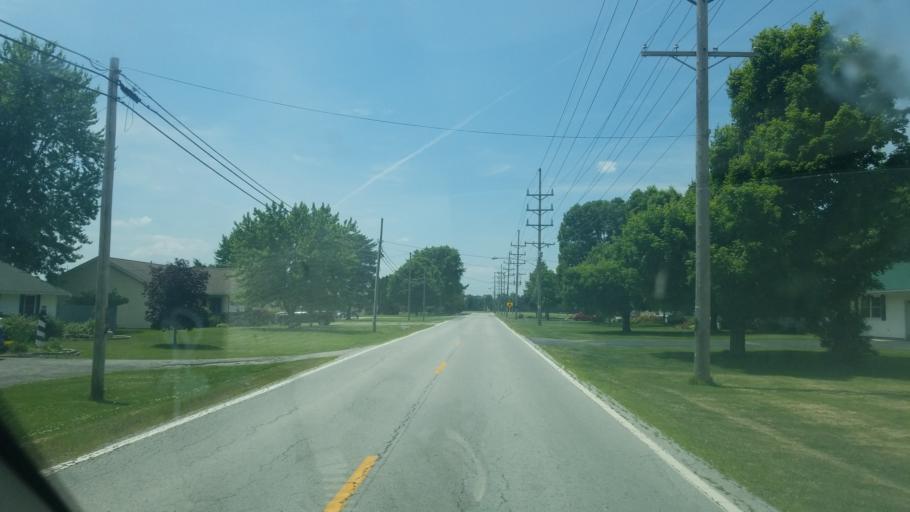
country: US
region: Ohio
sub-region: Hancock County
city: Arlington
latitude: 40.7831
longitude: -83.6485
